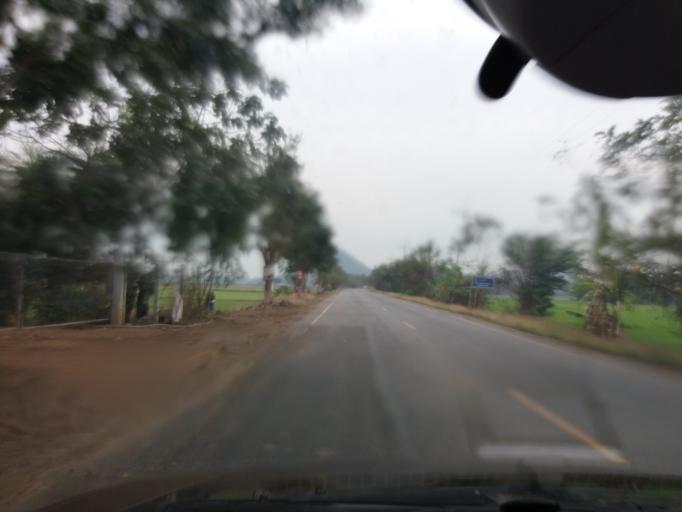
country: TH
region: Suphan Buri
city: Doembang Nangbuat
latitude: 14.8372
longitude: 100.1269
